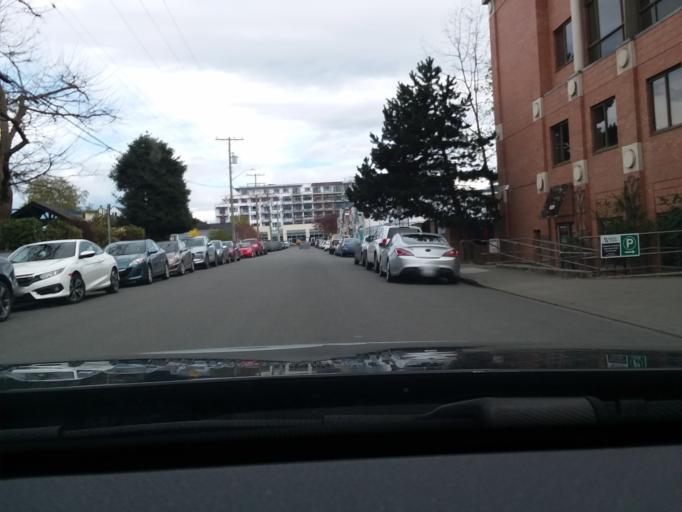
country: CA
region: British Columbia
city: Victoria
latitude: 48.4281
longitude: -123.3585
